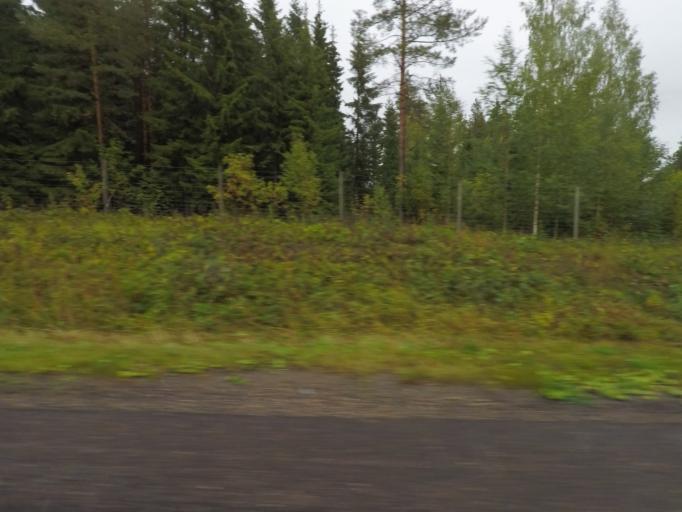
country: FI
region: Northern Savo
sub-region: Varkaus
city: Varkaus
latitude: 62.2376
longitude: 27.8897
